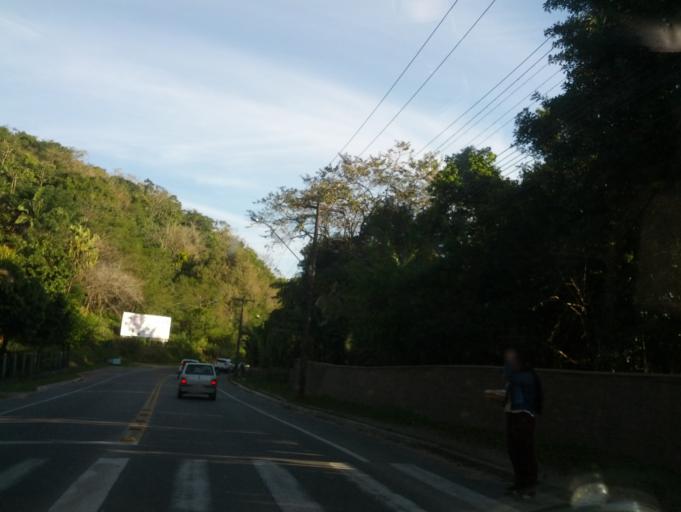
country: BR
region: Santa Catarina
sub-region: Indaial
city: Indaial
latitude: -26.8872
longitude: -49.2220
